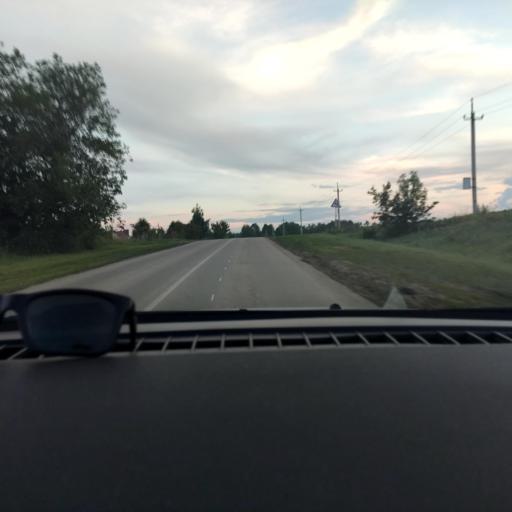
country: RU
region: Samara
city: Dubovyy Umet
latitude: 53.0415
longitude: 50.1765
